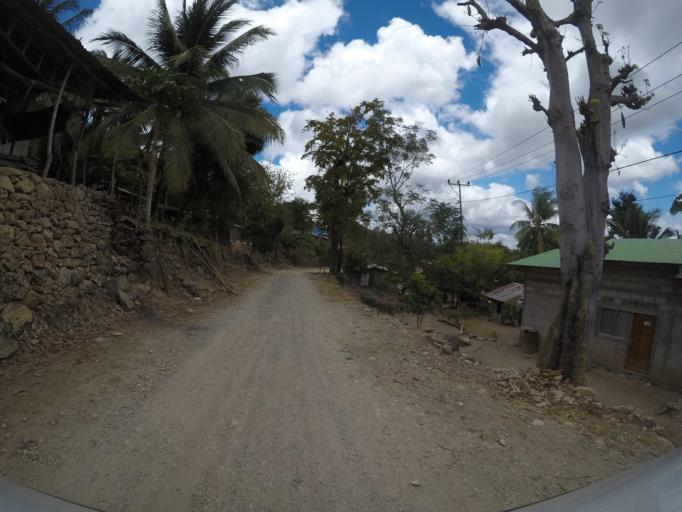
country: TL
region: Lautem
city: Lospalos
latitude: -8.3785
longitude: 126.9239
